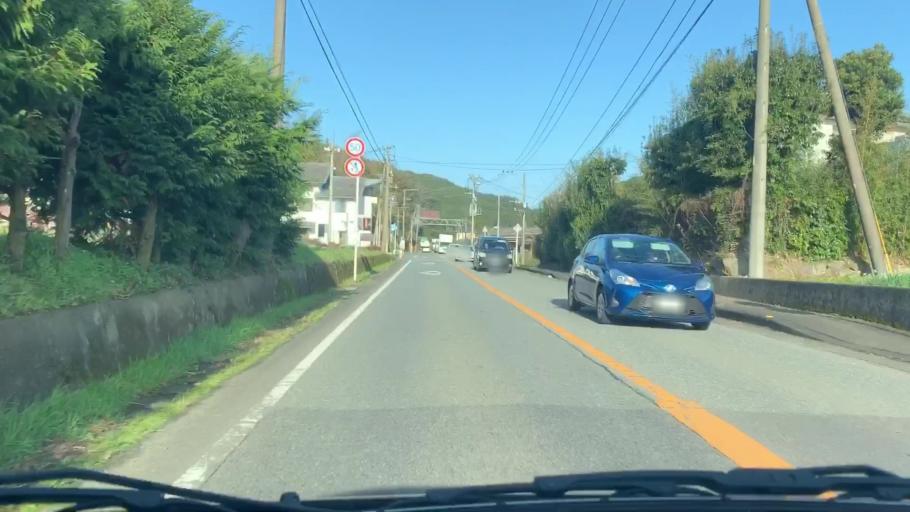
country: JP
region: Saga Prefecture
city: Takeocho-takeo
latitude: 33.2300
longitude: 130.0184
